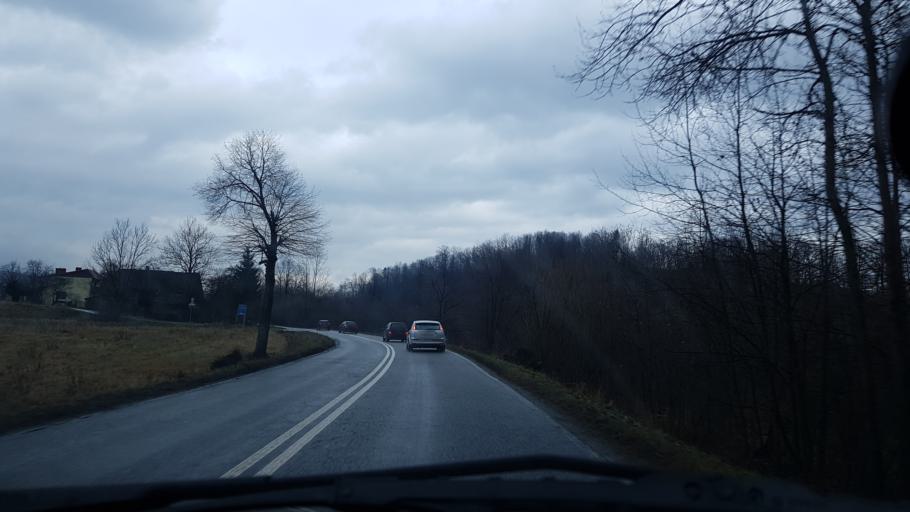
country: PL
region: Silesian Voivodeship
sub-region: Powiat zywiecki
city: Lekawica
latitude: 49.7115
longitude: 19.2582
